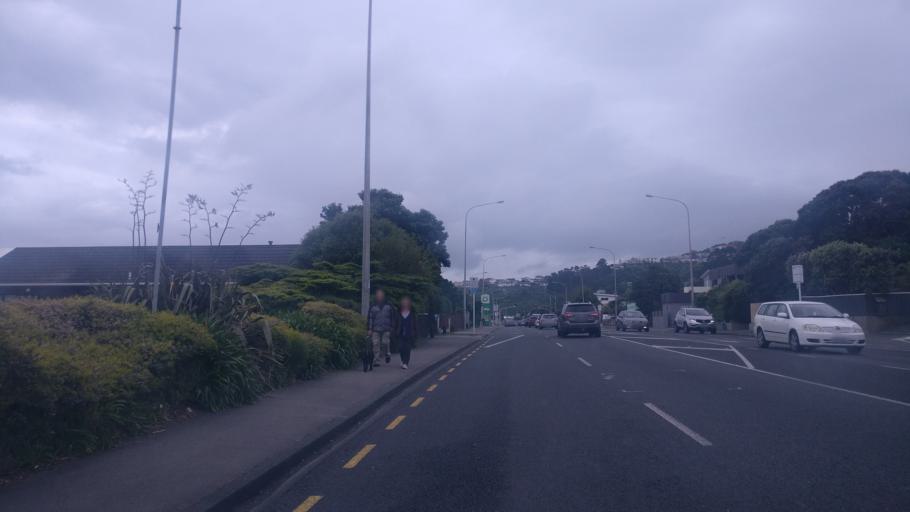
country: NZ
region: Wellington
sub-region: Porirua City
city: Porirua
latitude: -41.0975
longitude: 174.8694
